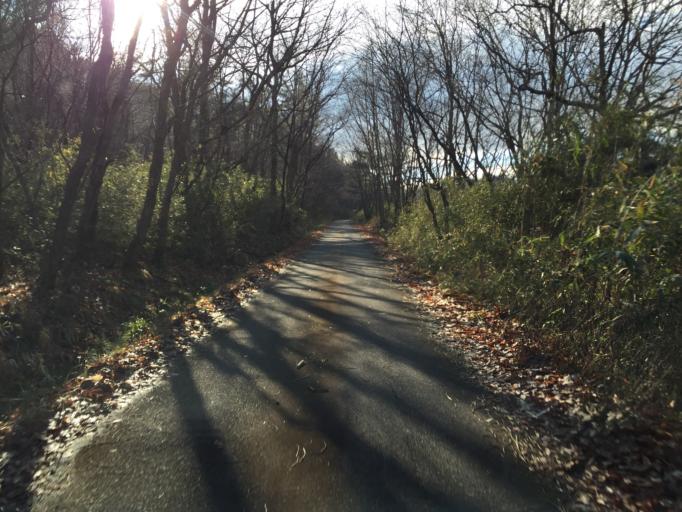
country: JP
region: Fukushima
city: Fukushima-shi
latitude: 37.6968
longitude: 140.4358
